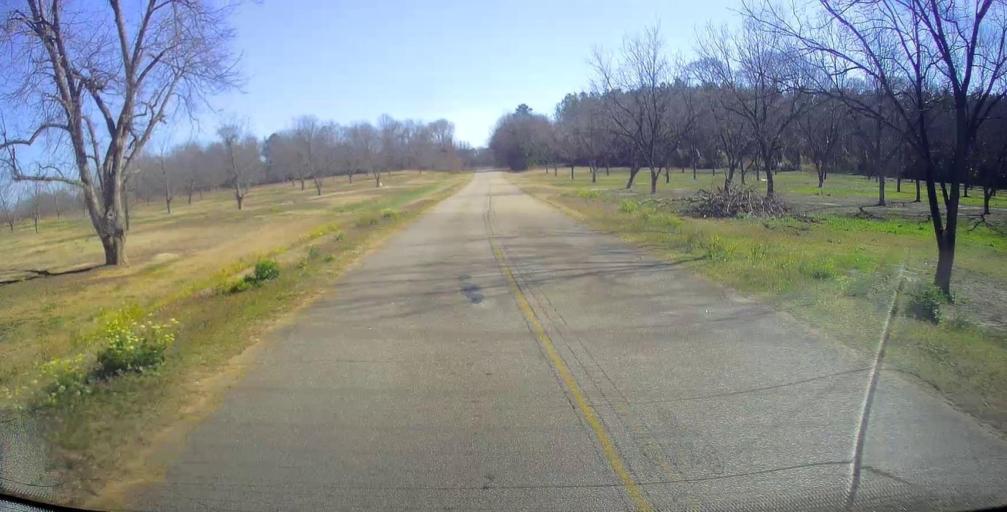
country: US
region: Georgia
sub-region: Peach County
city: Fort Valley
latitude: 32.6373
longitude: -83.8574
